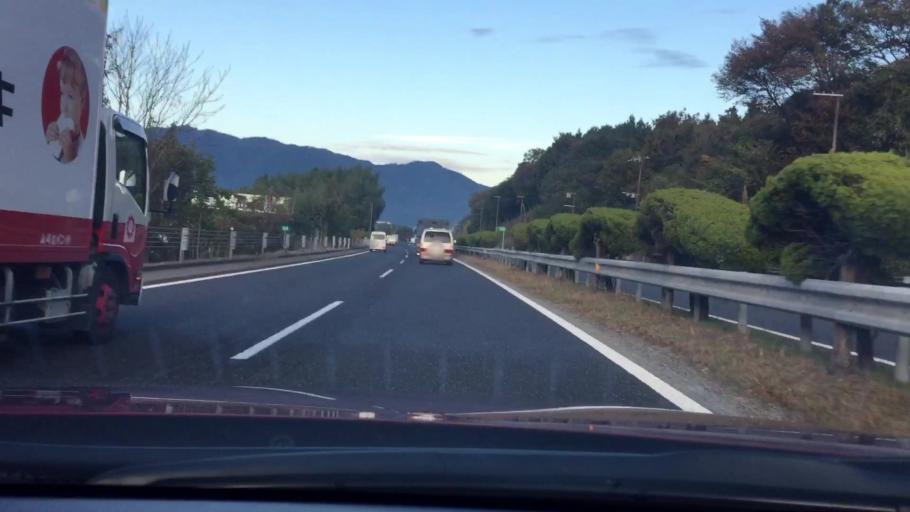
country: JP
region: Hyogo
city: Yamazakicho-nakabirose
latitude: 34.9945
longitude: 134.5694
